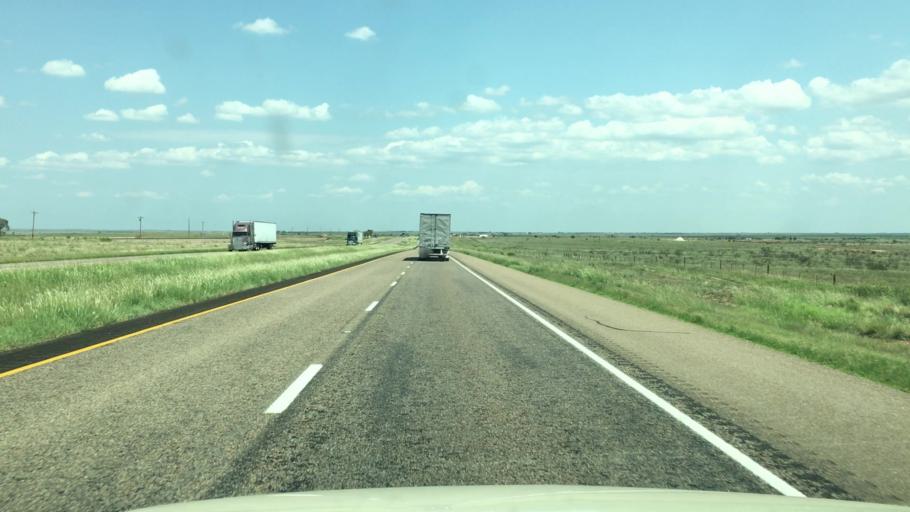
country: US
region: Texas
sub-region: Armstrong County
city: Claude
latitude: 35.0325
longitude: -101.1461
